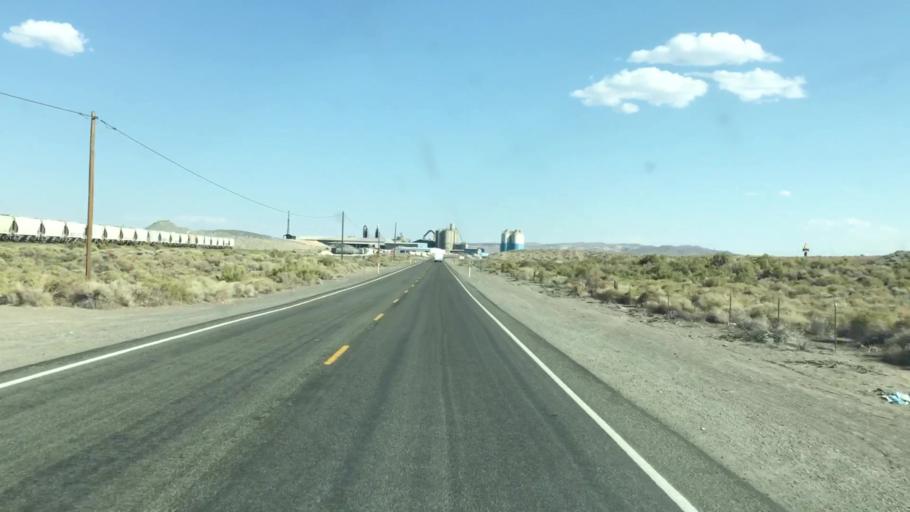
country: US
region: Nevada
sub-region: Lyon County
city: Fernley
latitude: 39.6269
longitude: -119.2728
